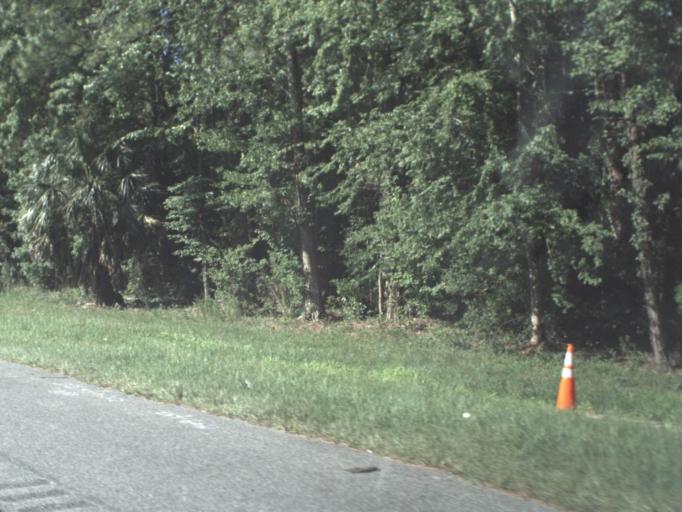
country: US
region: Florida
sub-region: Saint Johns County
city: Villano Beach
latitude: 30.0041
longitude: -81.4728
